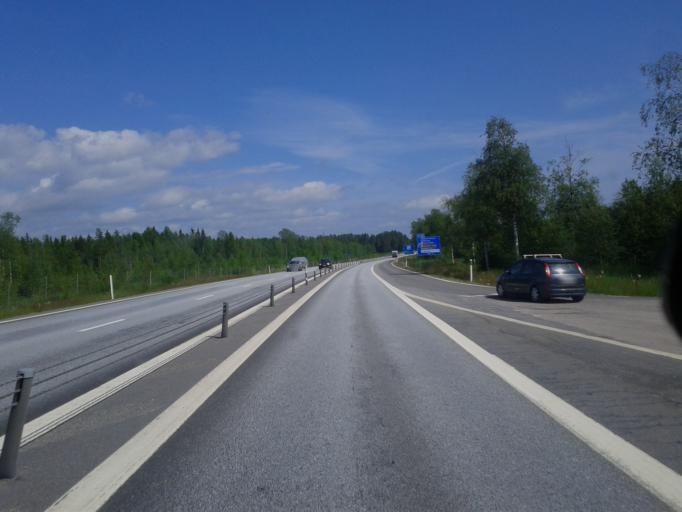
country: SE
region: Vaesterbotten
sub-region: Nordmalings Kommun
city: Nordmaling
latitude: 63.5730
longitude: 19.4428
